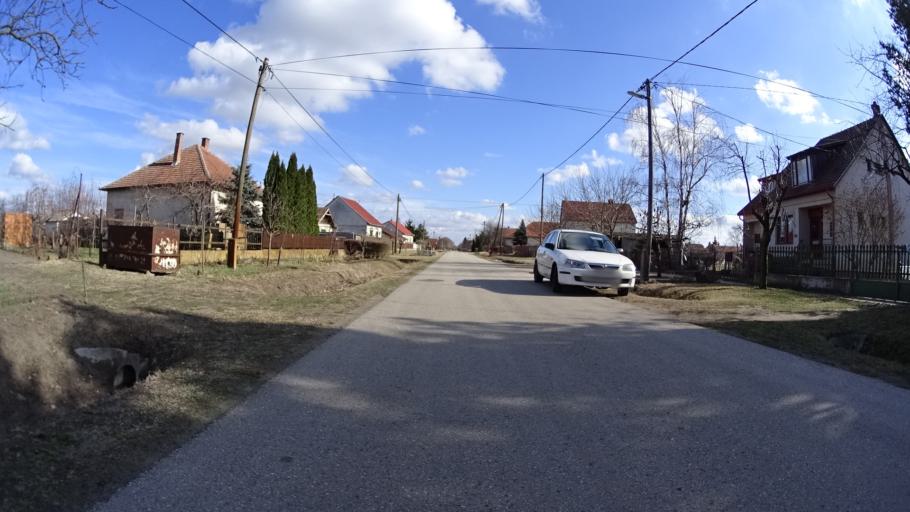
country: HU
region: Bacs-Kiskun
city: Tiszakecske
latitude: 46.9416
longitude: 20.0863
